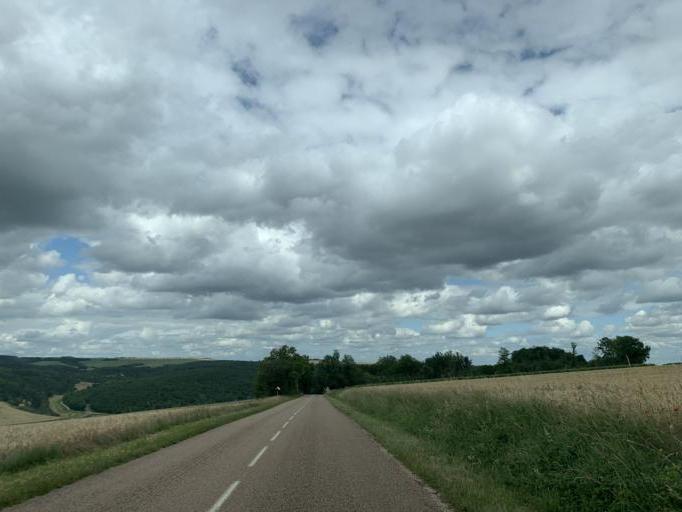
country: FR
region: Bourgogne
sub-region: Departement de l'Yonne
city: Saint-Bris-le-Vineux
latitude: 47.7200
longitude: 3.6831
